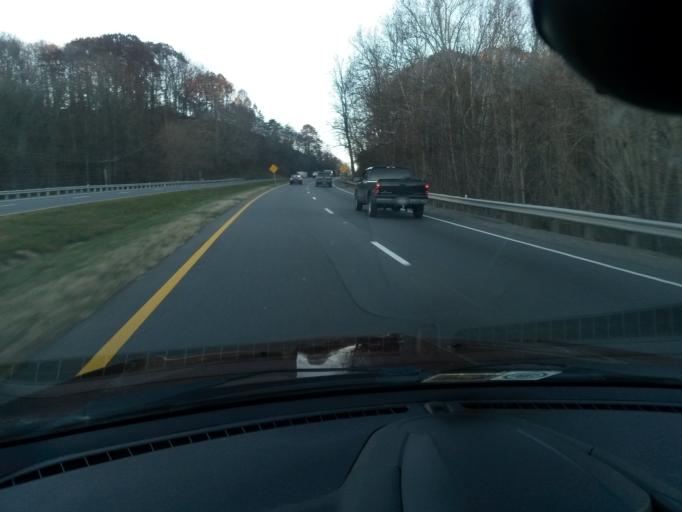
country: US
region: Virginia
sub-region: Franklin County
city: Rocky Mount
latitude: 37.0374
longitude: -79.8756
